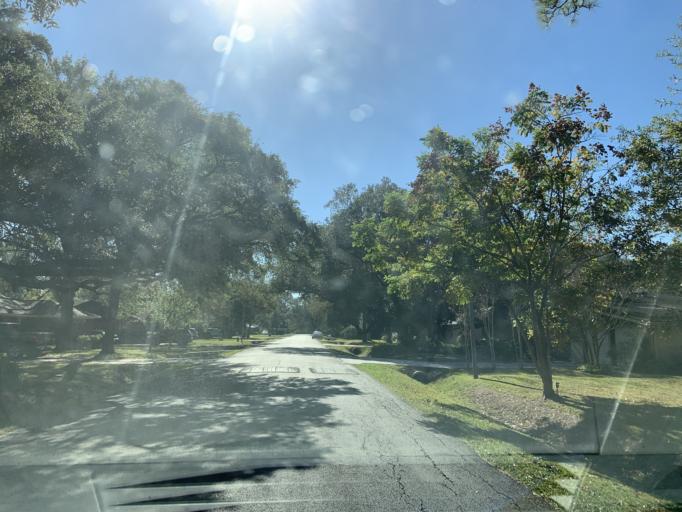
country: US
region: Texas
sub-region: Harris County
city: Bellaire
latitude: 29.6805
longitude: -95.5118
